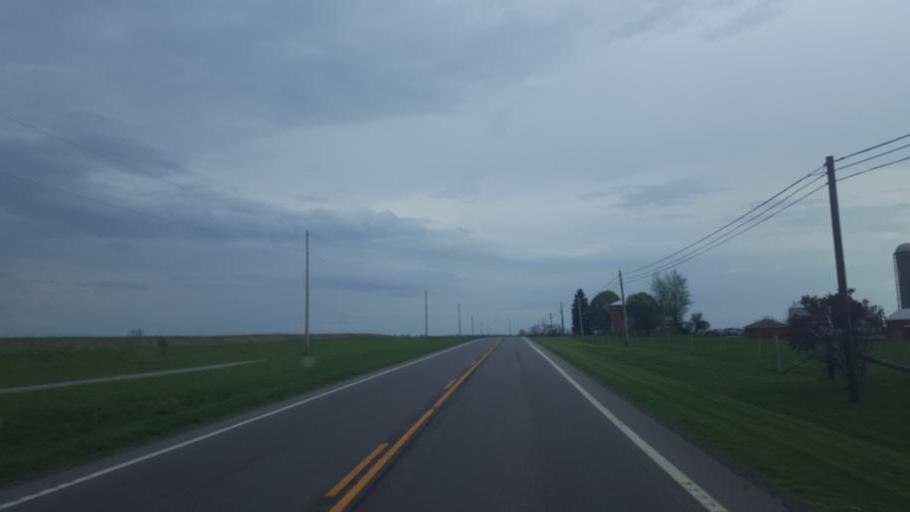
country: US
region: Ohio
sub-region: Wyandot County
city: Carey
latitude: 40.9845
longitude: -83.3824
